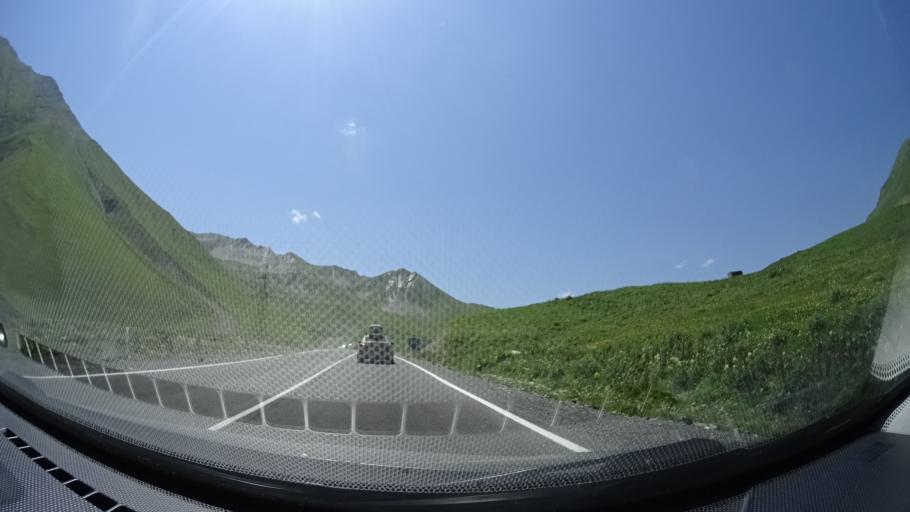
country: GE
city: Gudauri
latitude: 42.5207
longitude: 44.4673
